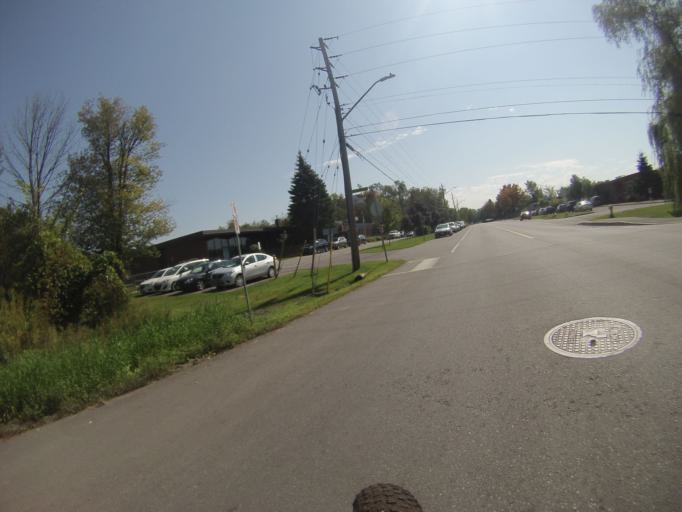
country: CA
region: Ontario
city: Ottawa
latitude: 45.3523
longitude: -75.6242
